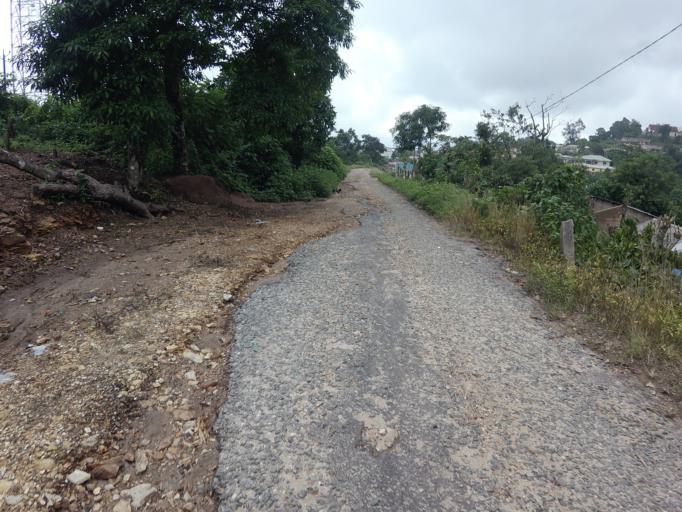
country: TG
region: Plateaux
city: Kpalime
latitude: 6.8423
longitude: 0.4337
